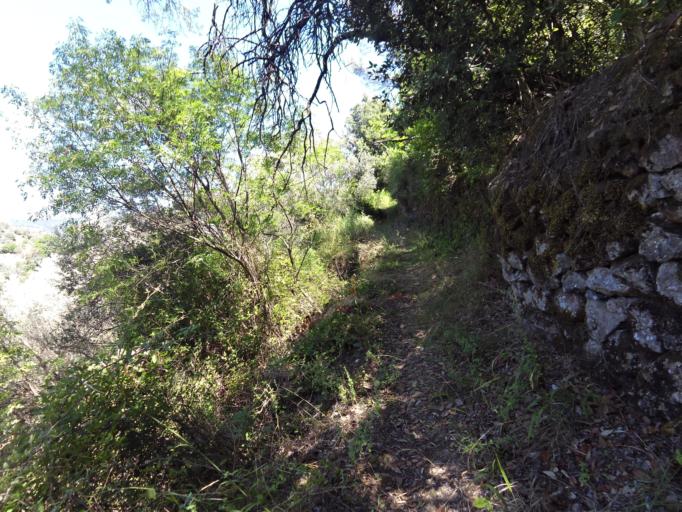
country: IT
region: Calabria
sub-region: Provincia di Reggio Calabria
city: Pazzano
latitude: 38.4766
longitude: 16.4442
